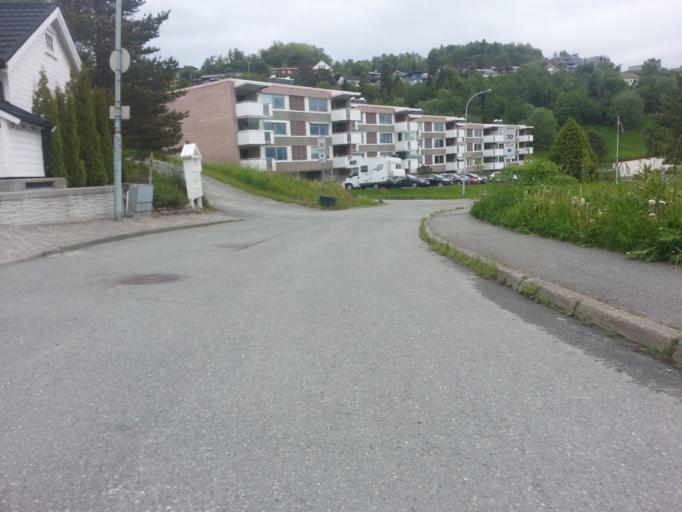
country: NO
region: Sor-Trondelag
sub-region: Trondheim
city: Trondheim
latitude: 63.4072
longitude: 10.4466
